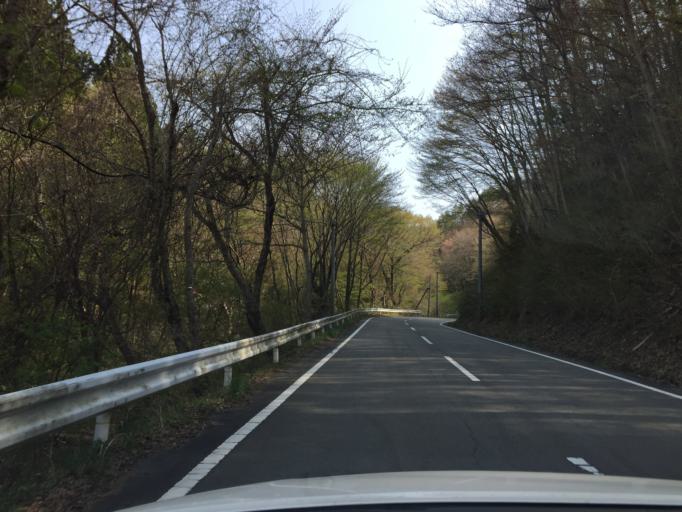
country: JP
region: Fukushima
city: Iwaki
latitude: 37.2385
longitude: 140.8460
